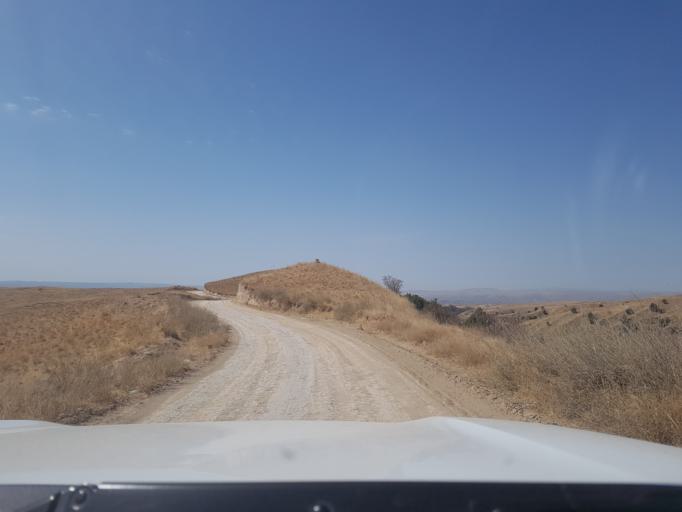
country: TM
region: Ahal
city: Baharly
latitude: 38.2792
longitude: 56.9210
